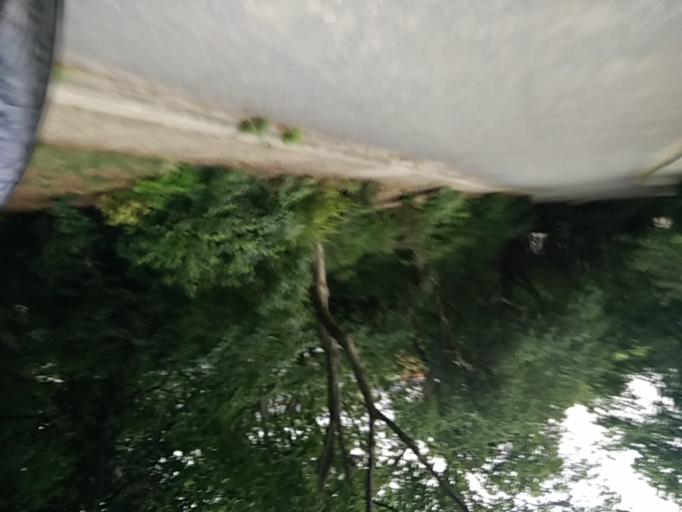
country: FR
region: Ile-de-France
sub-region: Departement de Seine-Saint-Denis
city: Le Pre-Saint-Gervais
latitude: 48.8808
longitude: 2.3870
